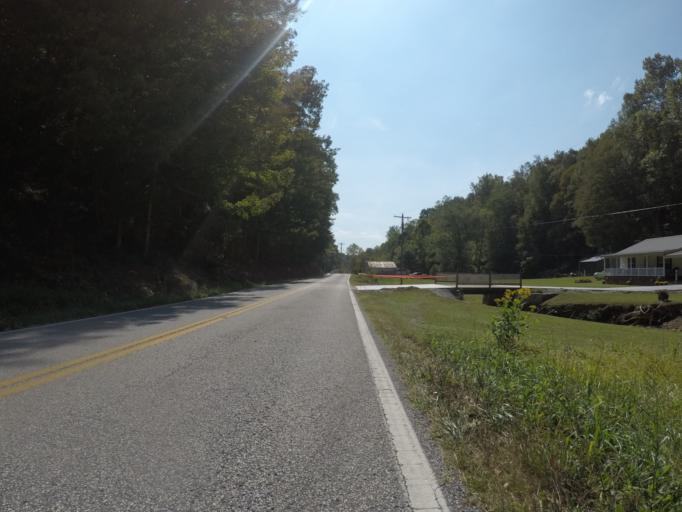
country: US
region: West Virginia
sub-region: Cabell County
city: Lesage
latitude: 38.5695
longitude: -82.4014
